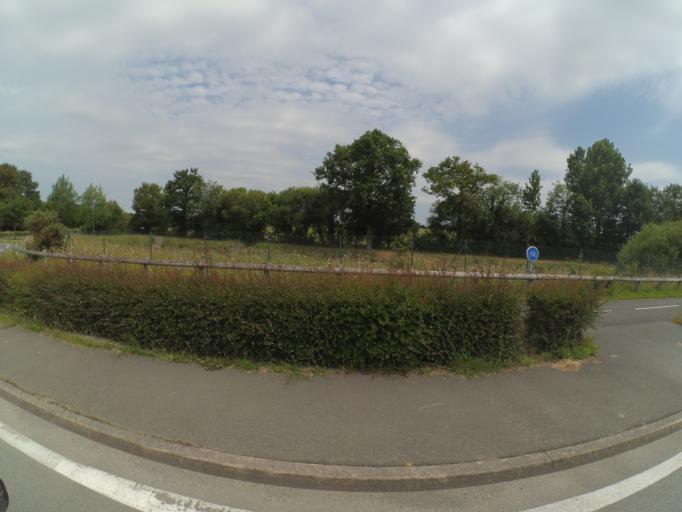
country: FR
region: Pays de la Loire
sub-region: Departement de la Vendee
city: Les Herbiers
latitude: 46.8456
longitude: -1.0147
